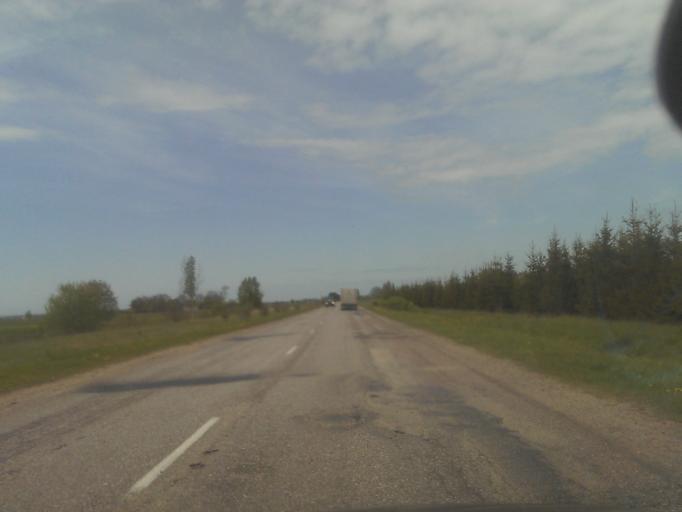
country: LV
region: Ventspils Rajons
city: Piltene
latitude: 57.1921
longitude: 21.6360
